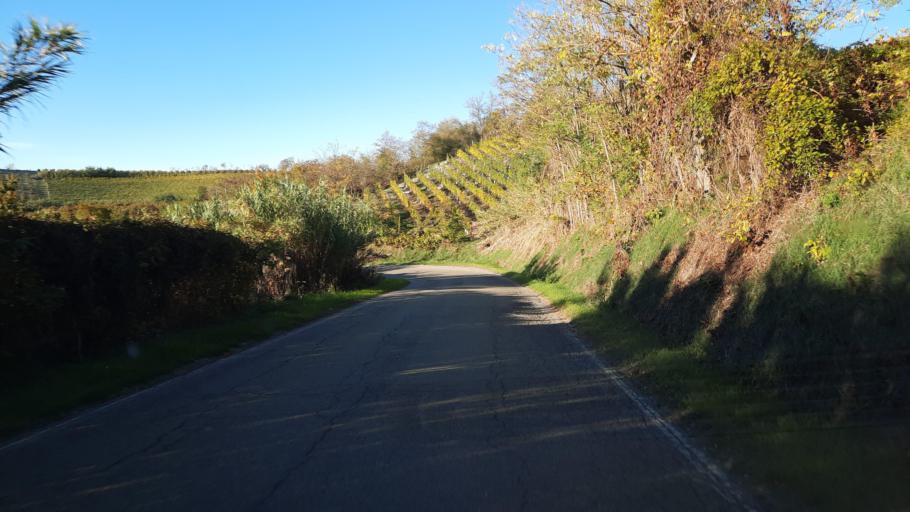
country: IT
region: Piedmont
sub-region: Provincia di Alessandria
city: Lu
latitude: 44.9923
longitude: 8.4803
